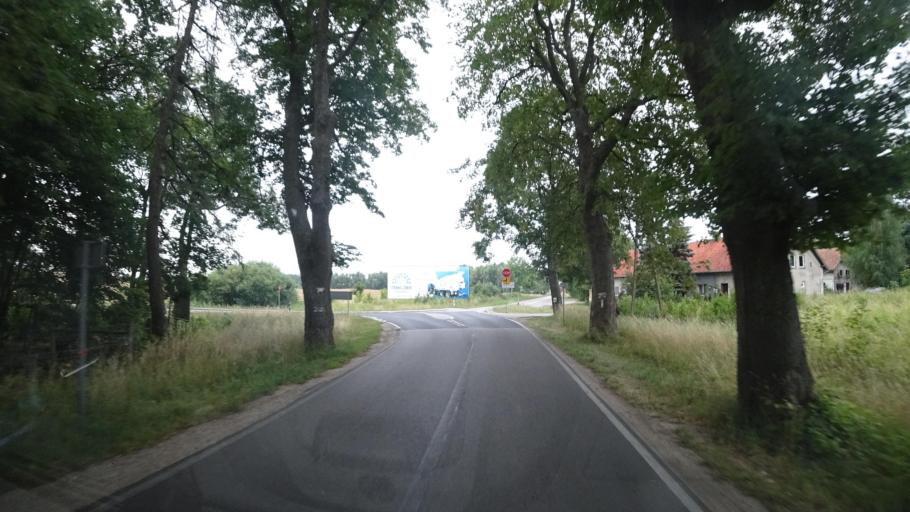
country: PL
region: Warmian-Masurian Voivodeship
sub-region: Powiat mragowski
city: Mikolajki
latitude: 53.8528
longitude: 21.6150
